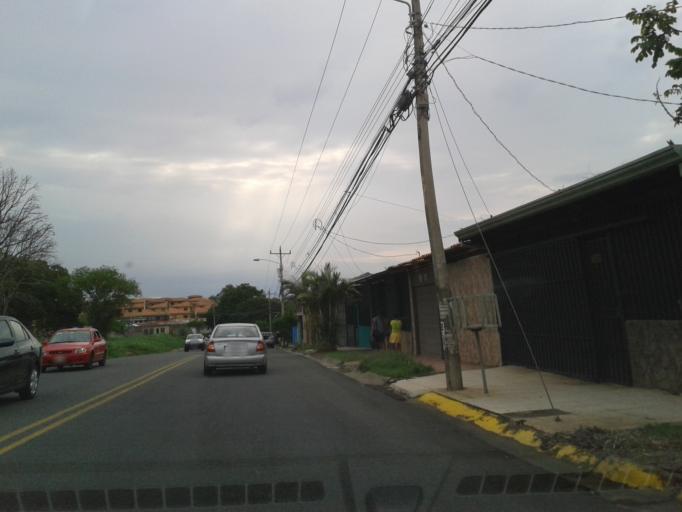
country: CR
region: Heredia
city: San Francisco
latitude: 9.9898
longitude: -84.1271
